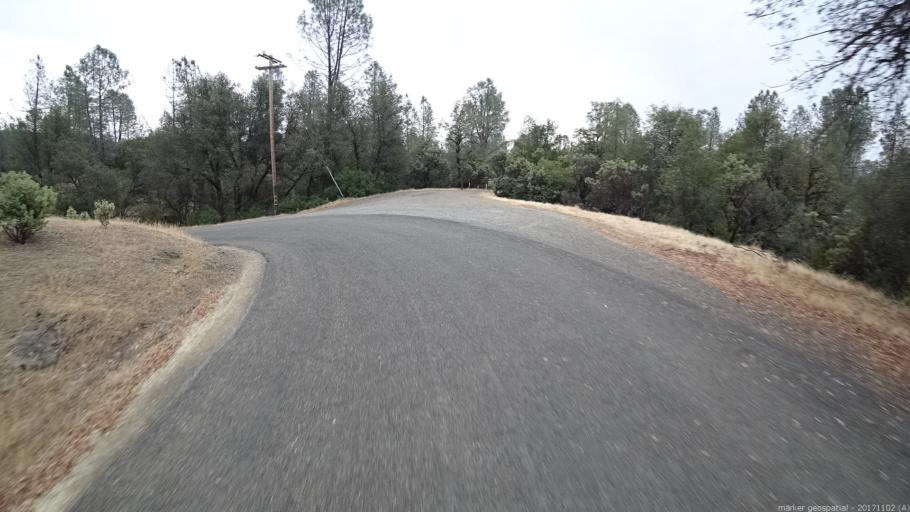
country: US
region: California
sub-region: Shasta County
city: Central Valley (historical)
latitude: 40.6620
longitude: -122.4378
